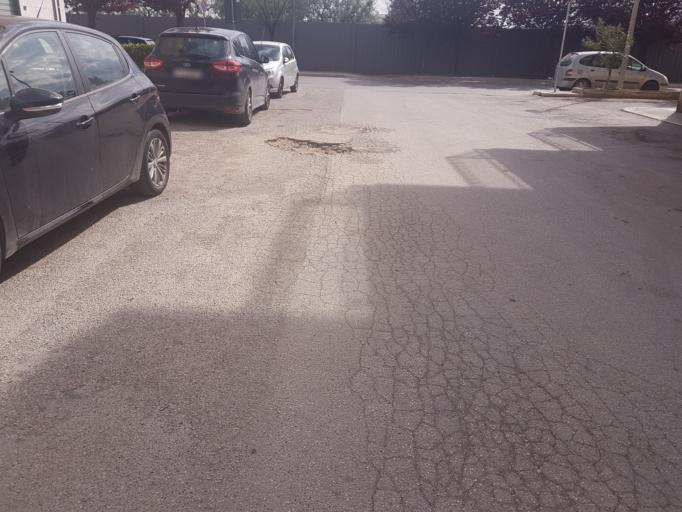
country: IT
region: Apulia
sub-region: Provincia di Bari
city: Corato
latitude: 41.1578
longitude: 16.4009
